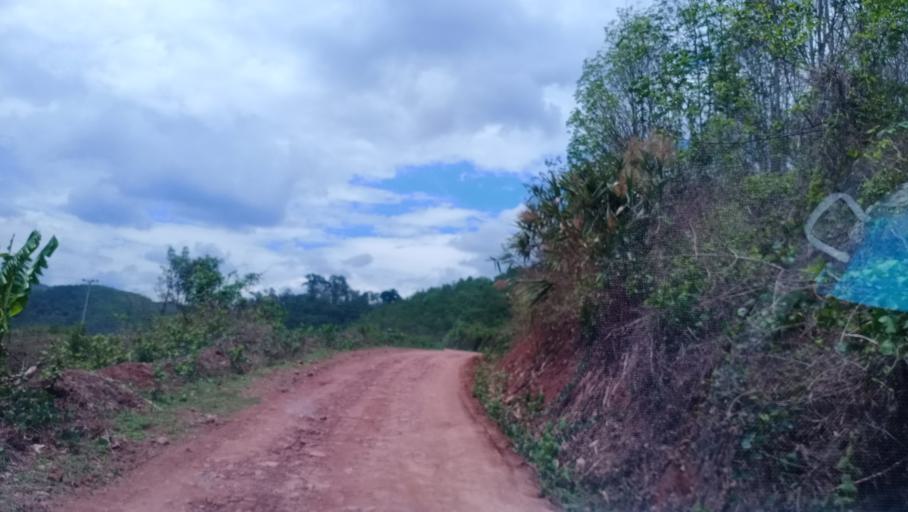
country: CN
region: Yunnan
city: Menglie
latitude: 22.1606
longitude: 101.7489
